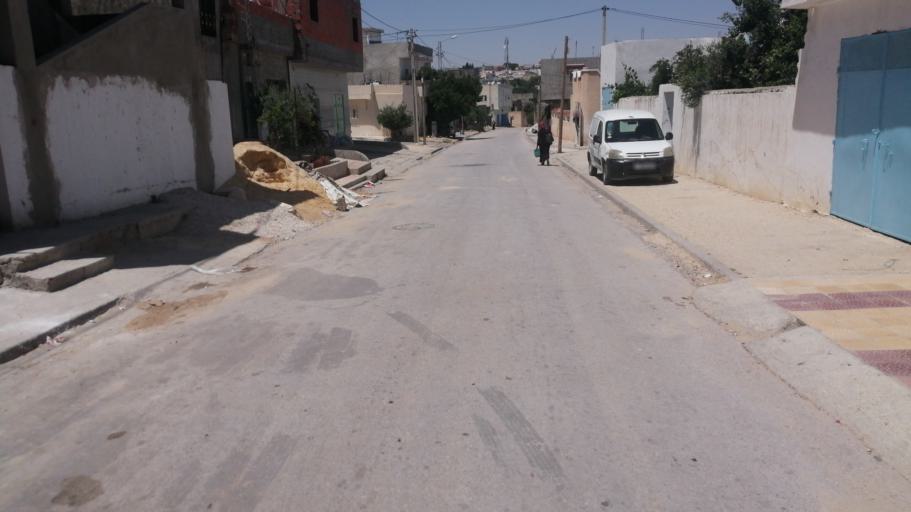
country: TN
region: Silyanah
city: Maktar
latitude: 35.8578
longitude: 9.2095
